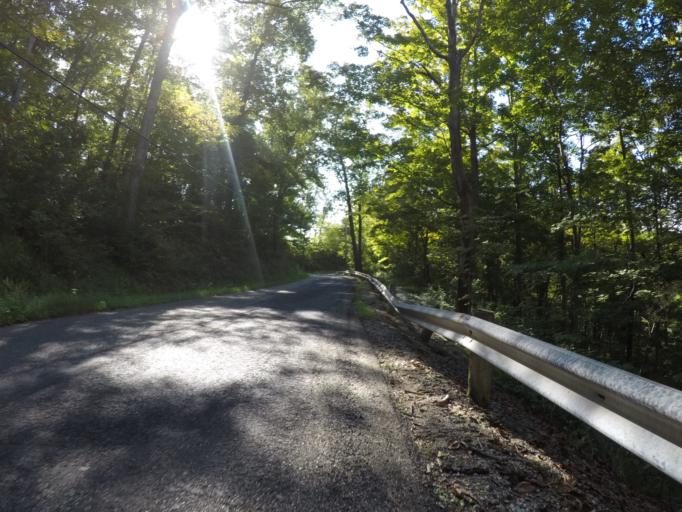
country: US
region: West Virginia
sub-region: Cabell County
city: Huntington
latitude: 38.4750
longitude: -82.4610
